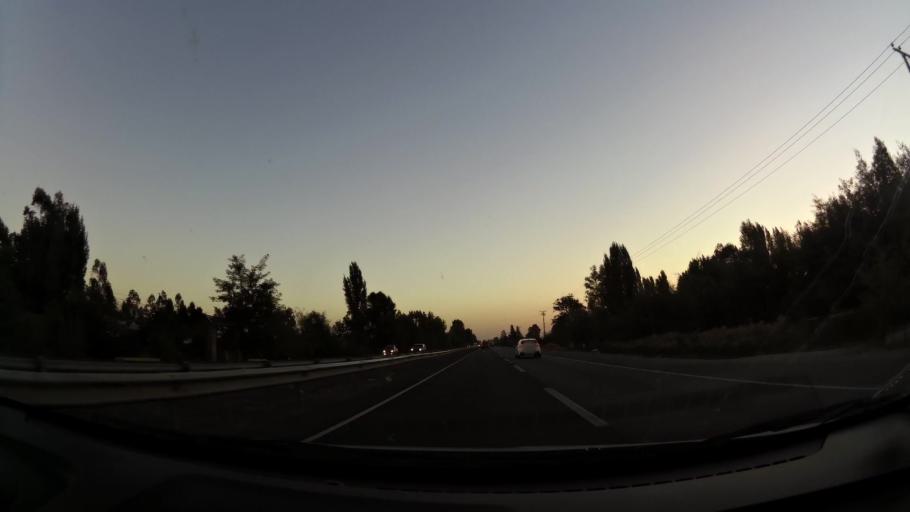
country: CL
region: Maule
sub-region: Provincia de Linares
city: Longavi
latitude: -35.9009
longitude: -71.6490
